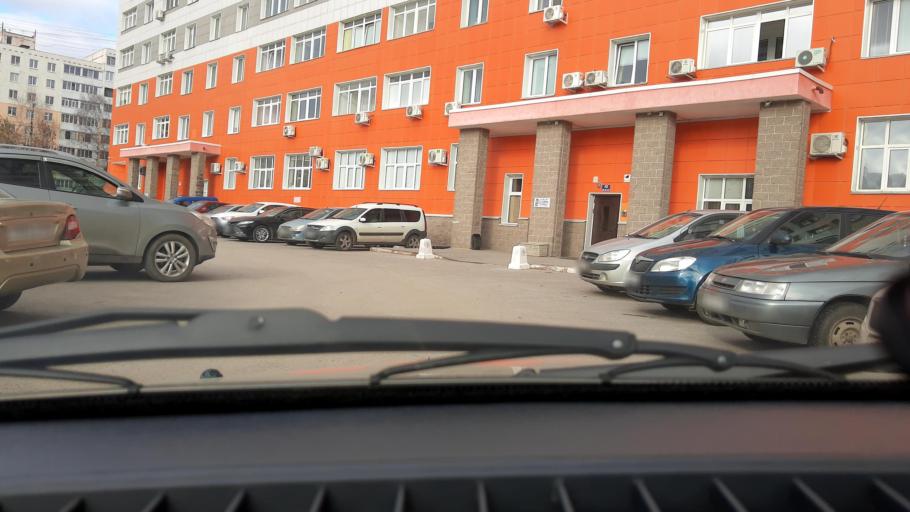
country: RU
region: Bashkortostan
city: Ufa
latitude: 54.7613
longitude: 56.0222
